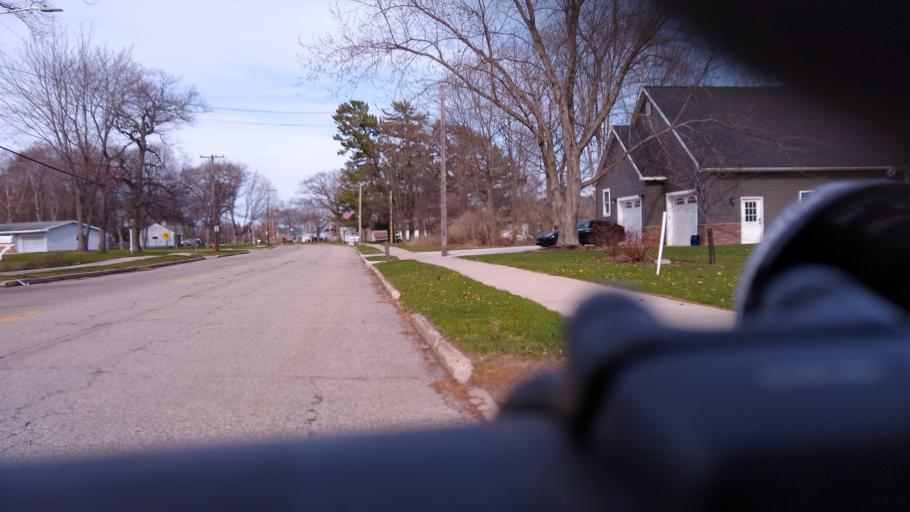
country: US
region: Michigan
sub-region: Delta County
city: Escanaba
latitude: 45.7169
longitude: -87.0757
